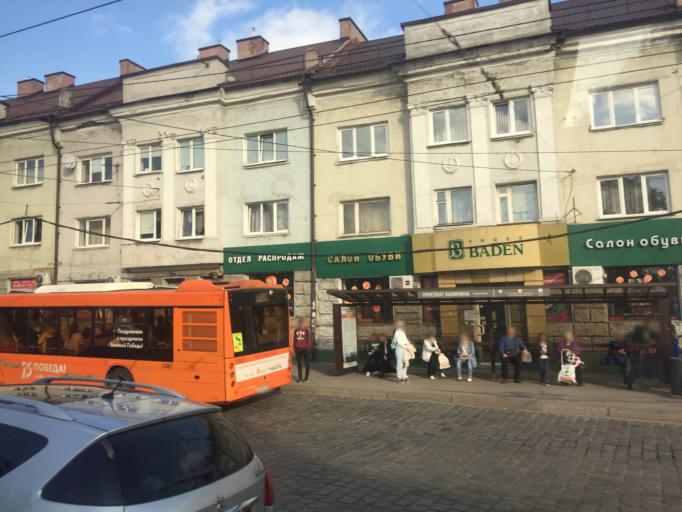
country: RU
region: Kaliningrad
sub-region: Gorod Kaliningrad
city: Kaliningrad
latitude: 54.6951
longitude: 20.5031
